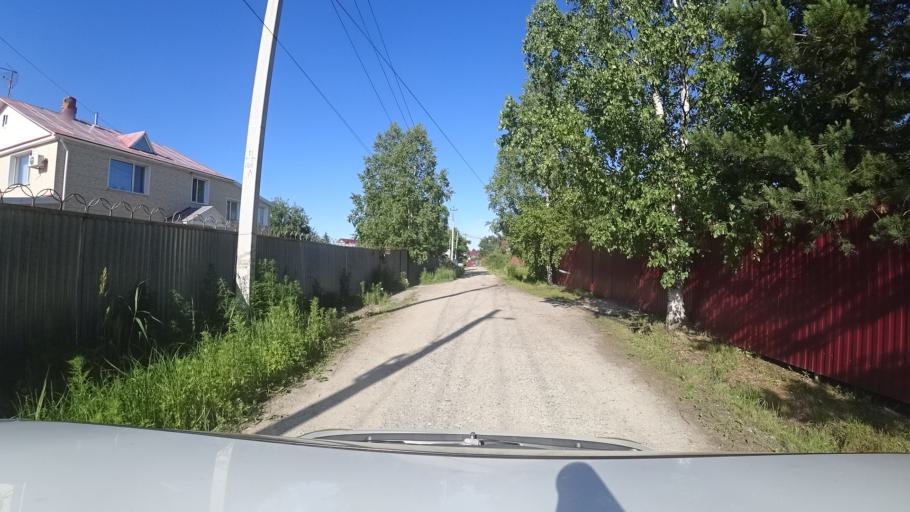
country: RU
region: Khabarovsk Krai
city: Topolevo
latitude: 48.5405
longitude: 135.1776
